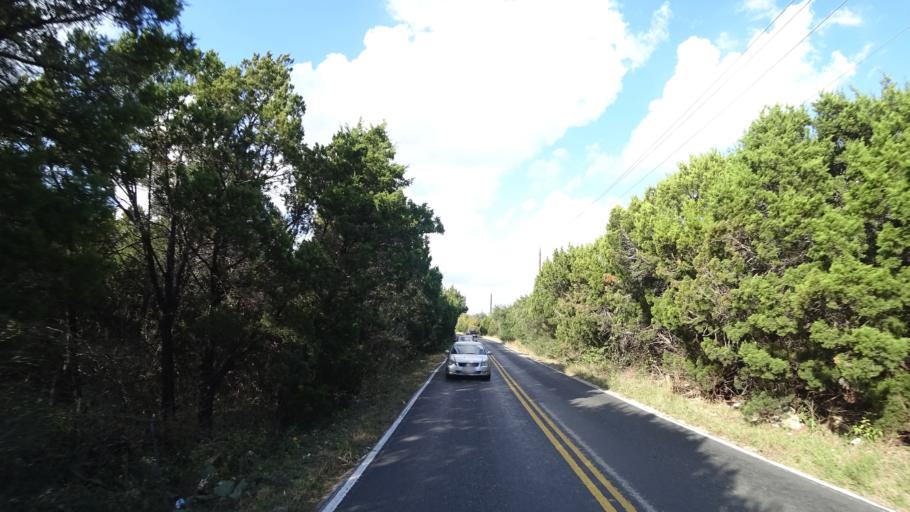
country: US
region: Texas
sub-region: Travis County
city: Barton Creek
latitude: 30.2597
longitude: -97.8884
